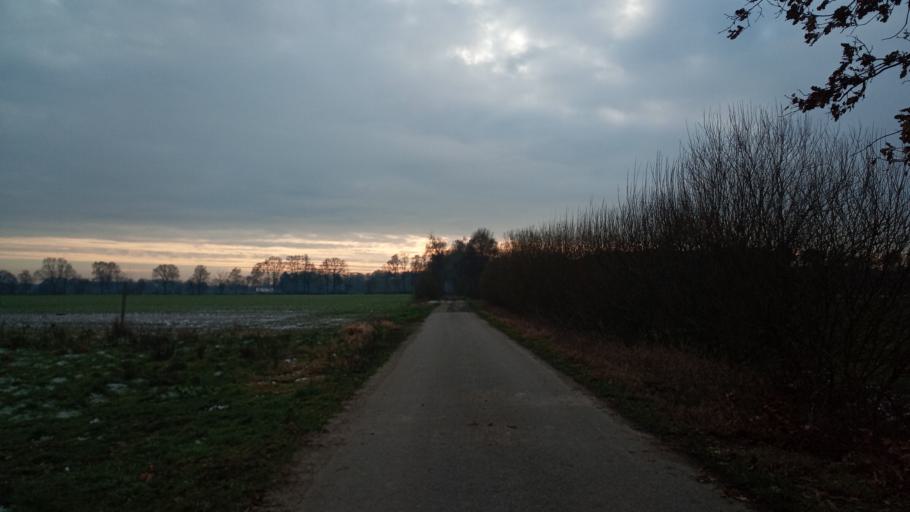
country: DE
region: Lower Saxony
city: Horstedt
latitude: 53.1631
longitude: 9.2501
